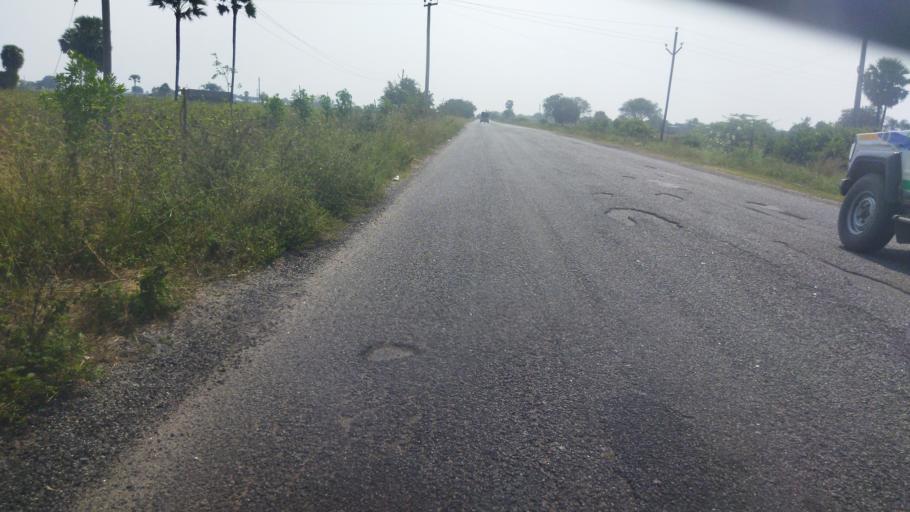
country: IN
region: Telangana
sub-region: Nalgonda
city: Nalgonda
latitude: 17.1017
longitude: 79.2835
